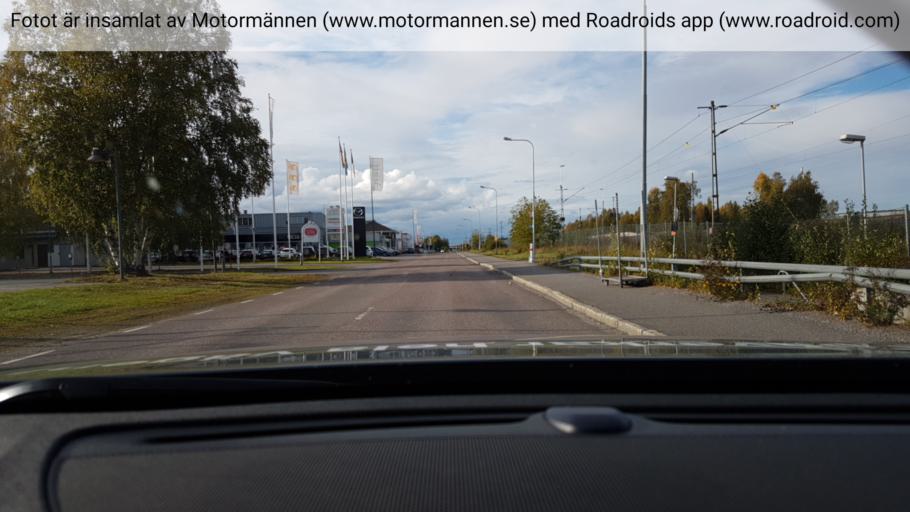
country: SE
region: Norrbotten
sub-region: Lulea Kommun
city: Bergnaset
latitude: 65.6088
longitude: 22.1240
